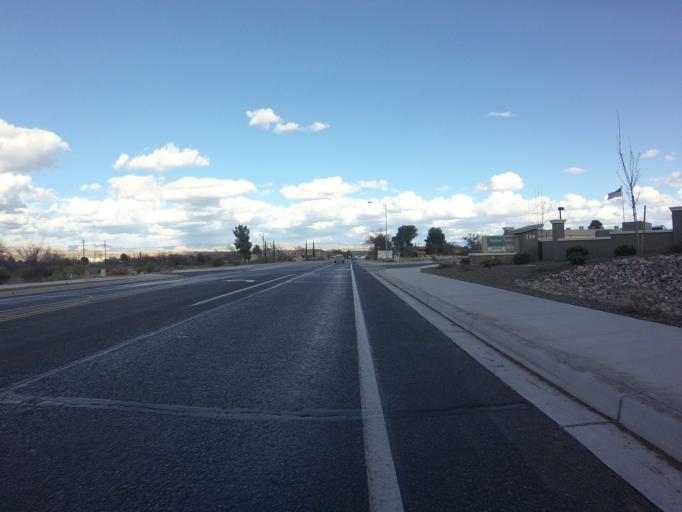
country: US
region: Arizona
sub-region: Yavapai County
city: Cottonwood
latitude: 34.7396
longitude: -112.0302
